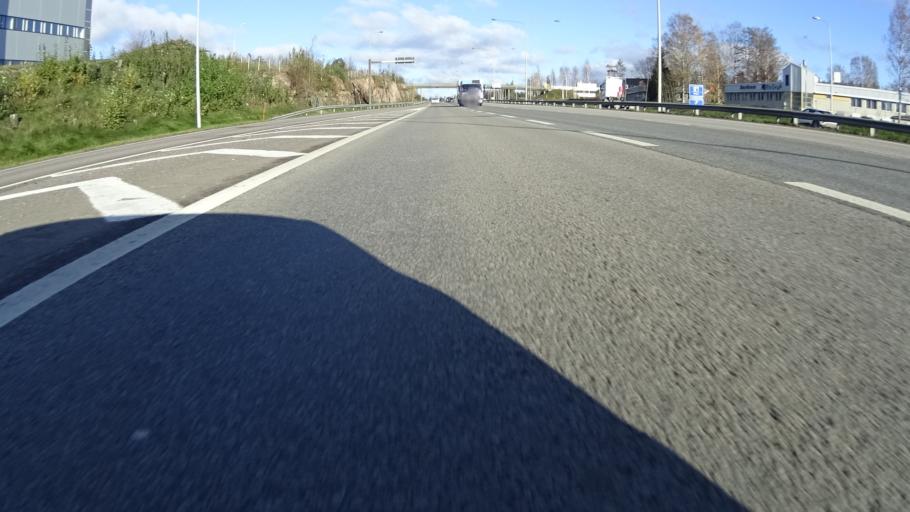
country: FI
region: Uusimaa
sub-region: Helsinki
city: Vantaa
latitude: 60.3026
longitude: 24.9915
